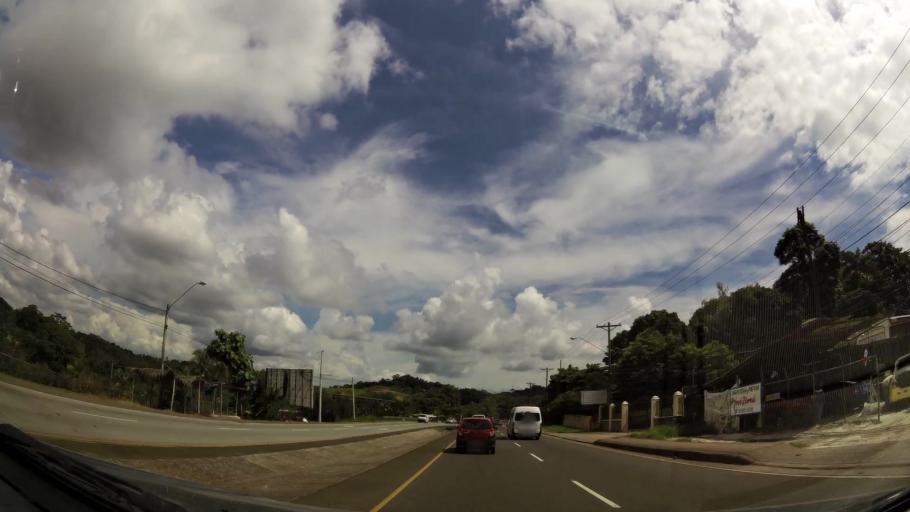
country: PA
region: Panama
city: Vista Alegre
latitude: 8.9326
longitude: -79.6981
